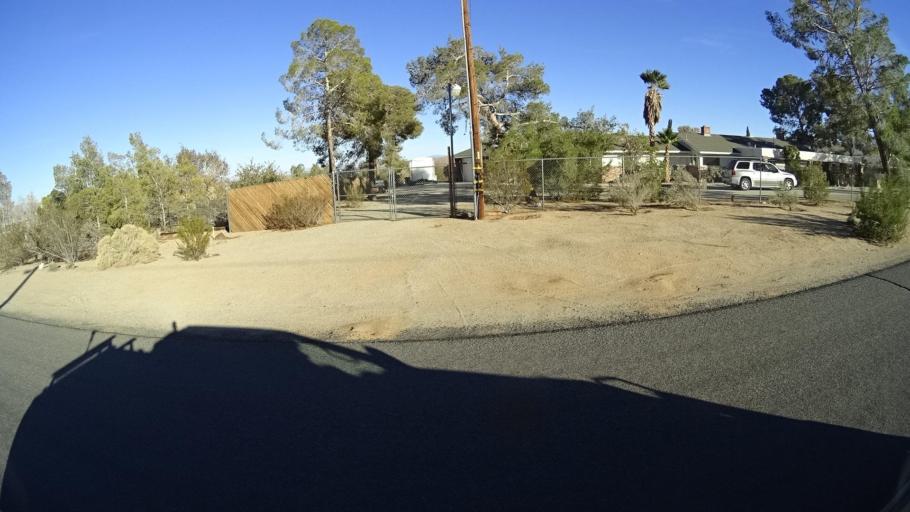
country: US
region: California
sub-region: Kern County
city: Ridgecrest
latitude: 35.5924
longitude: -117.6977
